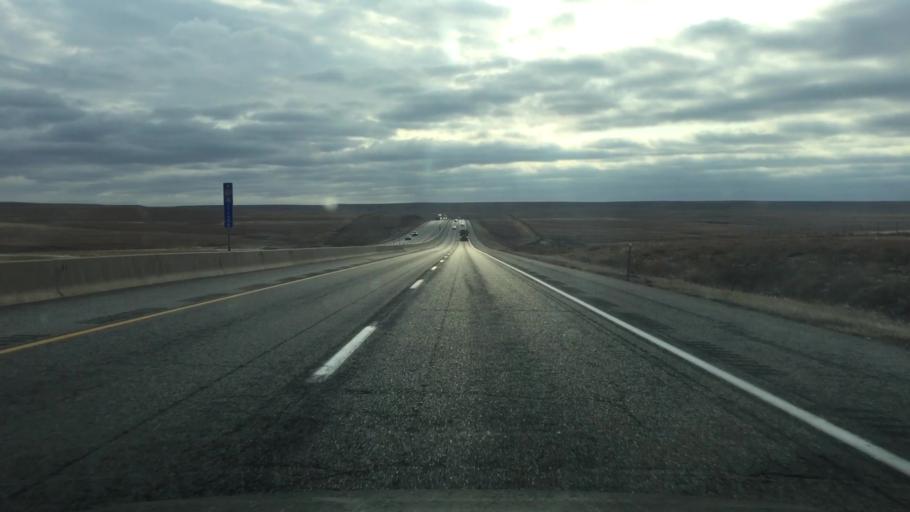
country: US
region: Kansas
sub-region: Chase County
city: Cottonwood Falls
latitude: 38.2629
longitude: -96.3845
